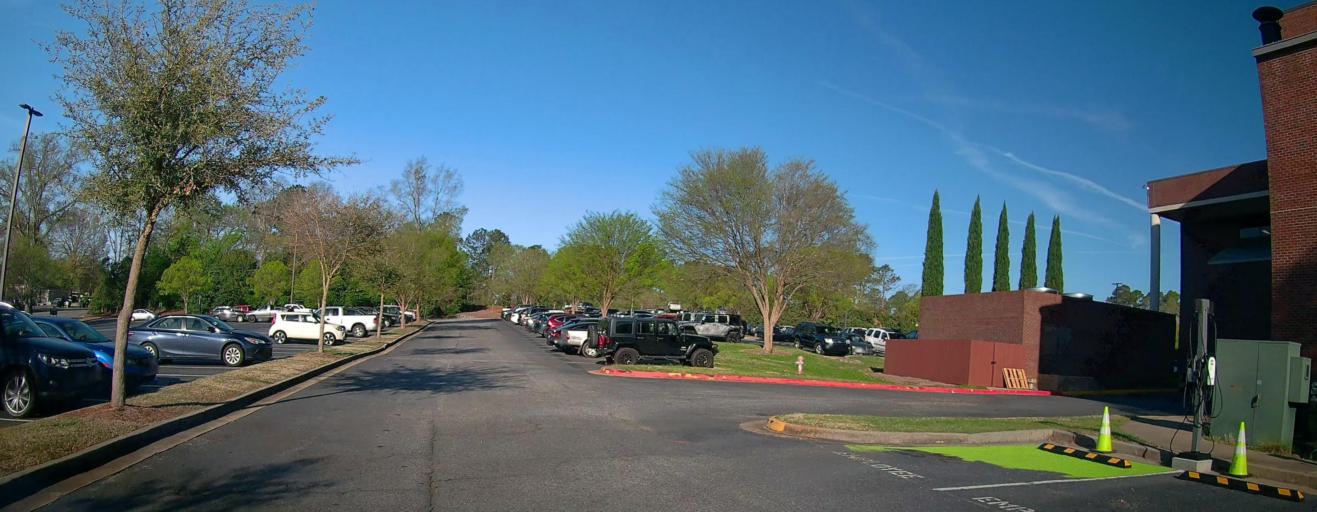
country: US
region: Georgia
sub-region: Baldwin County
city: Milledgeville
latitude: 33.0762
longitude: -83.2334
